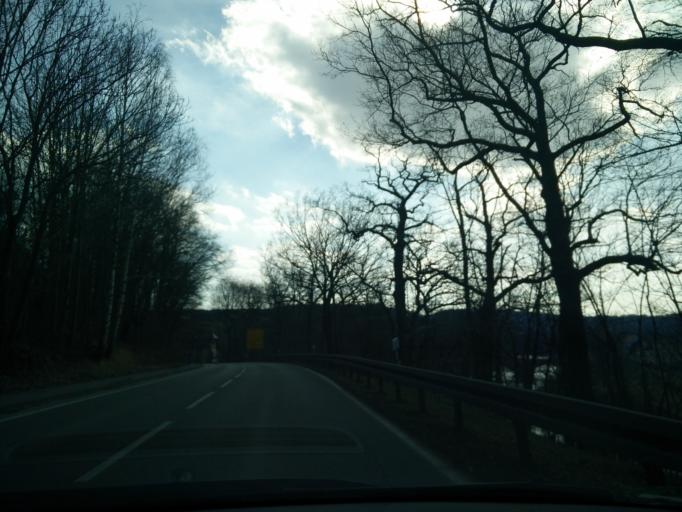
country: DE
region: Saxony
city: Seelitz
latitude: 51.0460
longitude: 12.8110
